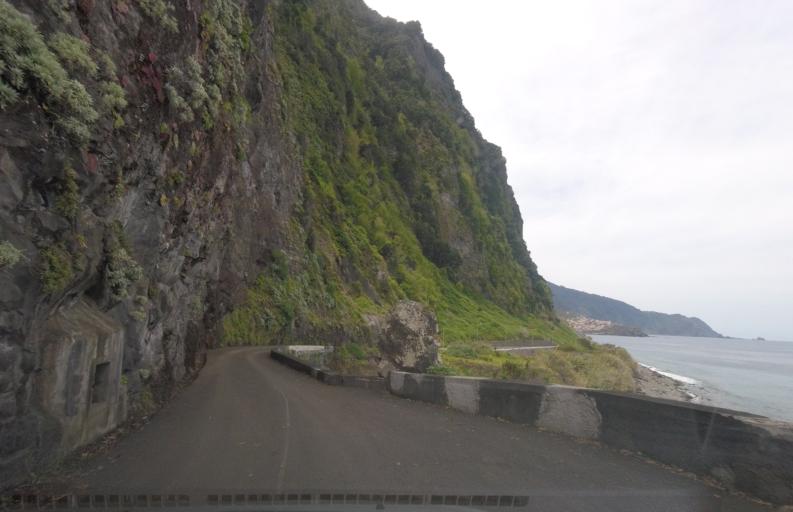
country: PT
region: Madeira
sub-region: Sao Vicente
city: Sao Vicente
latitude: 32.8140
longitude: -17.0767
